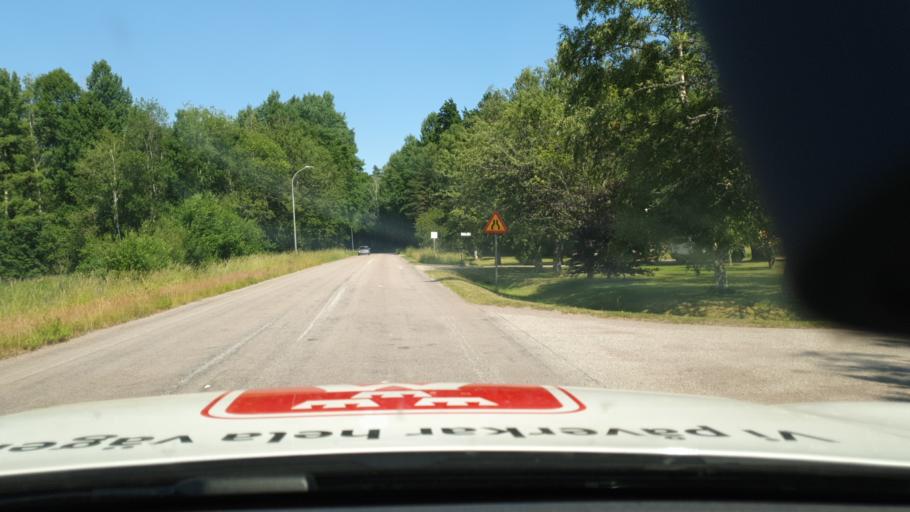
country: SE
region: Vaestra Goetaland
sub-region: Mariestads Kommun
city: Mariestad
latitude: 58.6492
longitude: 13.9053
